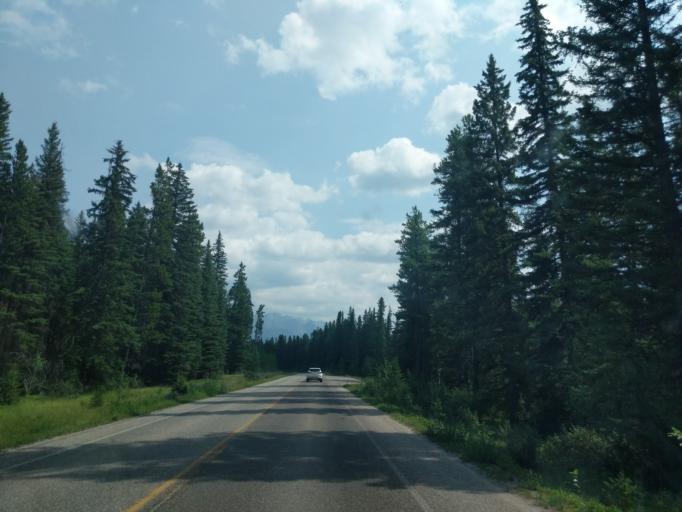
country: CA
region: Alberta
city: Banff
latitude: 51.2105
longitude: -115.7577
